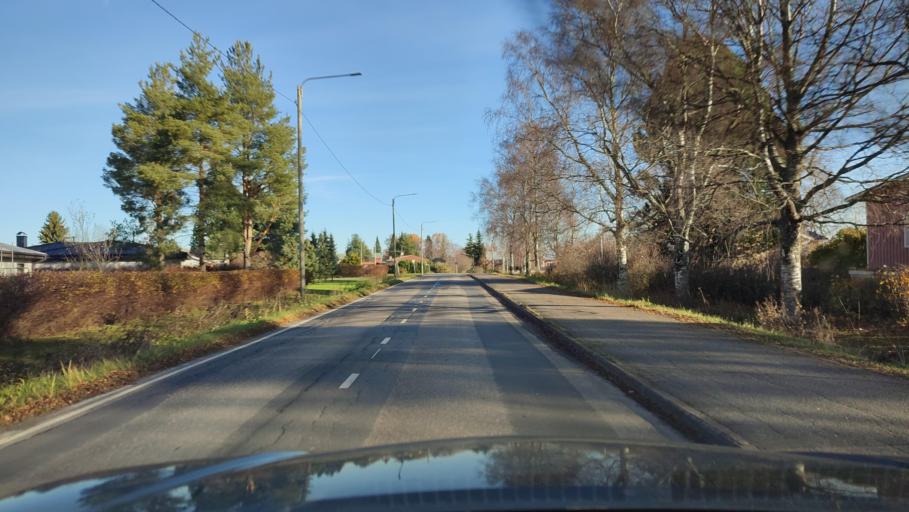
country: FI
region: Southern Ostrobothnia
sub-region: Suupohja
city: Teuva
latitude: 62.4878
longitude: 21.7537
